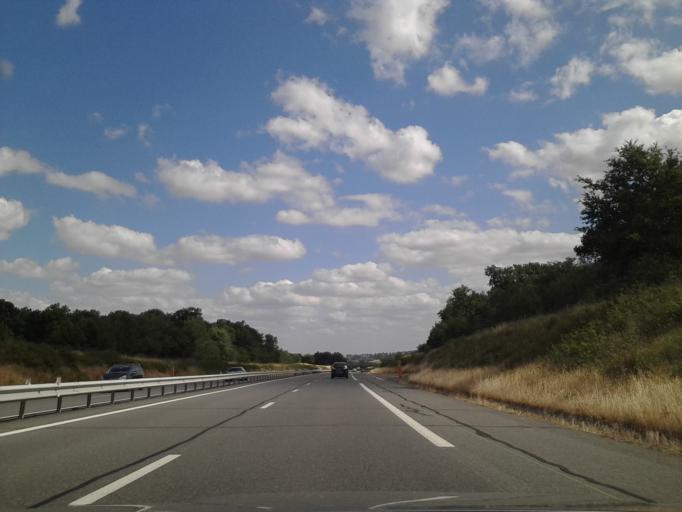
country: FR
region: Auvergne
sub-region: Departement de l'Allier
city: Vallon-en-Sully
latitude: 46.5626
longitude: 2.5430
